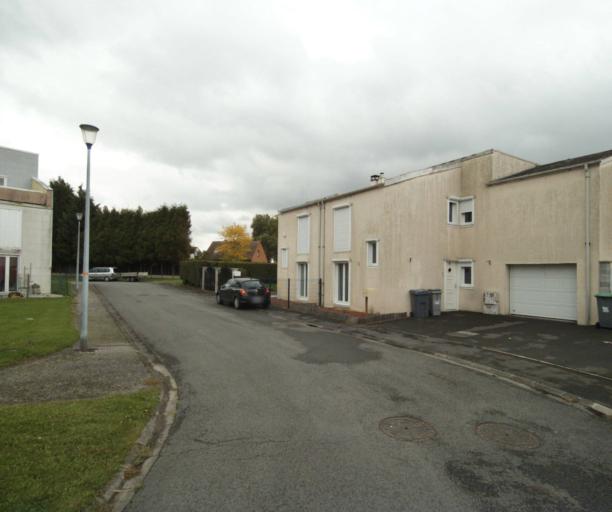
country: FR
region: Nord-Pas-de-Calais
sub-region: Departement du Nord
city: Wavrin
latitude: 50.5669
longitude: 2.9444
